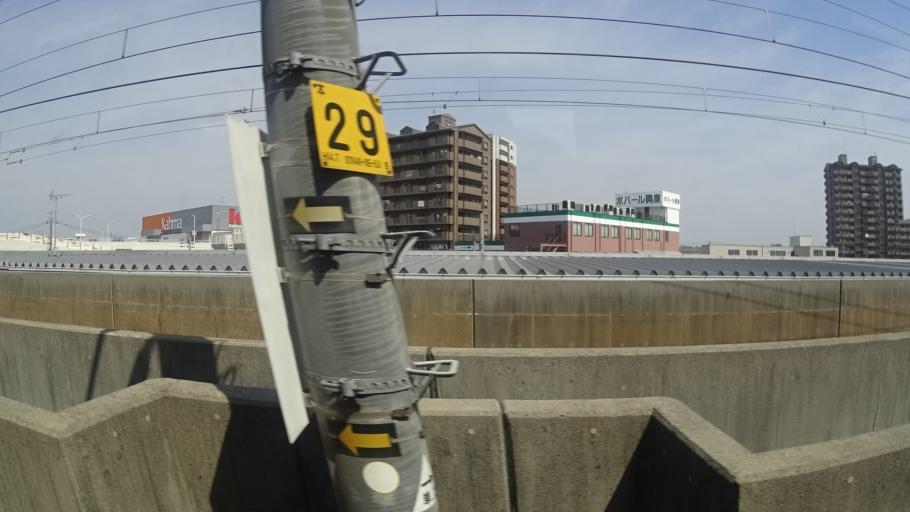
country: JP
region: Aichi
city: Kanie
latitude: 35.1471
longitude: 136.8448
